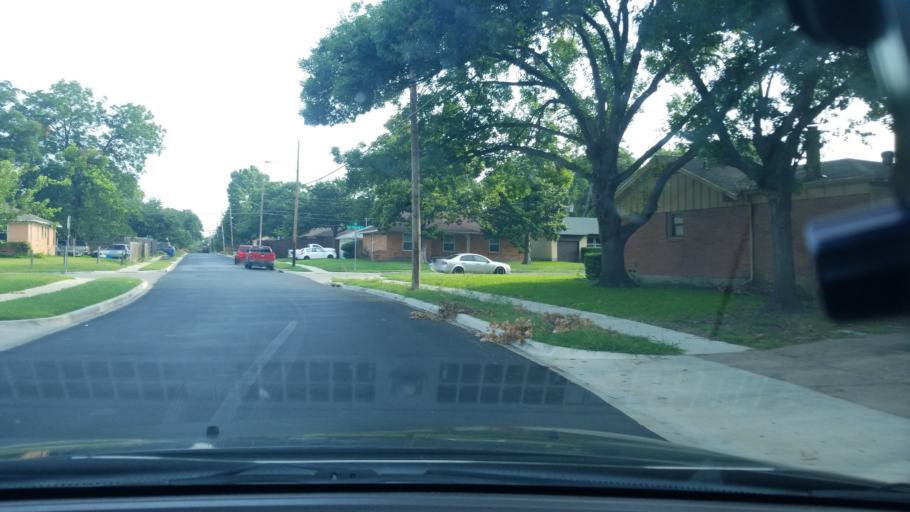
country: US
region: Texas
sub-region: Dallas County
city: Garland
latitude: 32.8300
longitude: -96.6638
